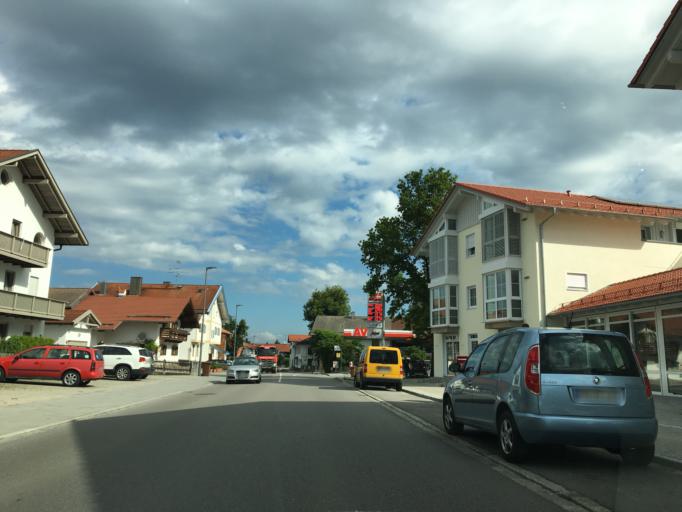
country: DE
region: Bavaria
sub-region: Upper Bavaria
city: Otterfing
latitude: 47.9075
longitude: 11.6761
